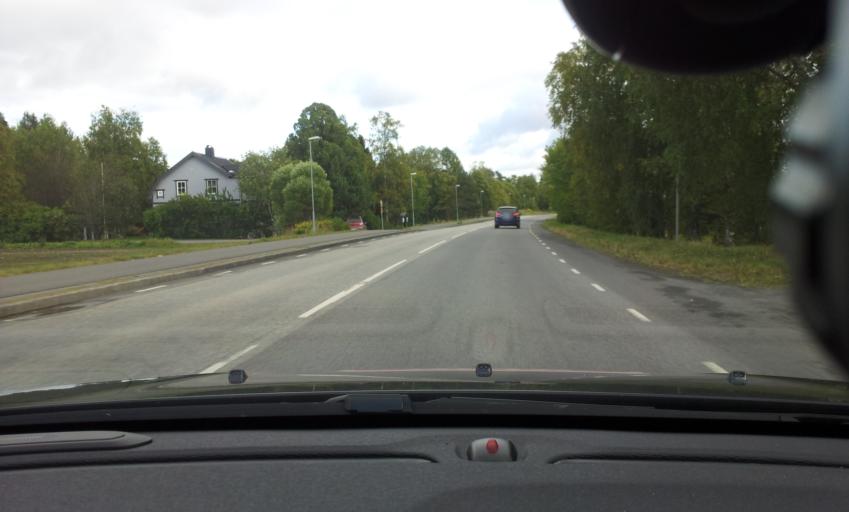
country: SE
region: Jaemtland
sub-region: OEstersunds Kommun
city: Ostersund
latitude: 63.1407
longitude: 14.7388
